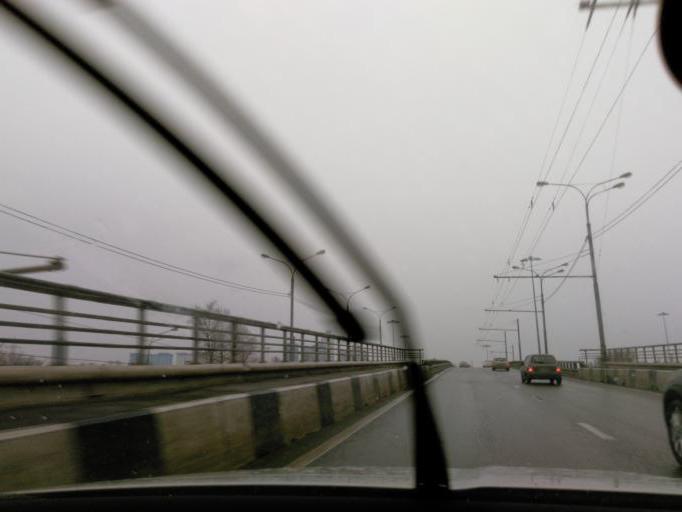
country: RU
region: Moscow
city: Pokrovskoye-Streshnevo
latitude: 55.8223
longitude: 37.4505
